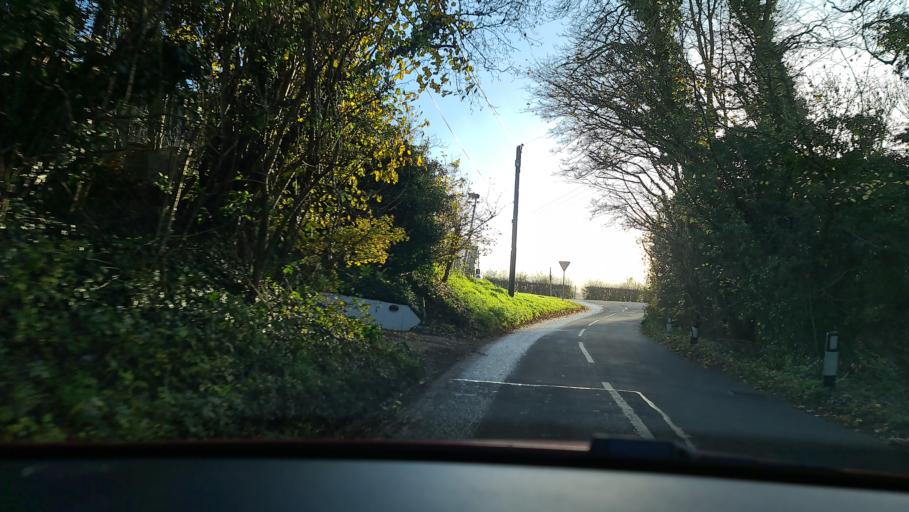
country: GB
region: England
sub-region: Buckinghamshire
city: Weston Turville
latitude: 51.7703
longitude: -0.7897
